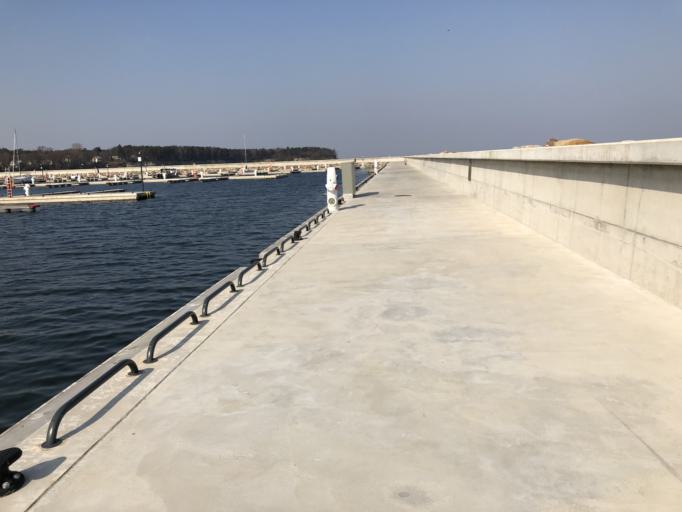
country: EE
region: Harju
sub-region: Harku vald
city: Tabasalu
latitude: 59.4523
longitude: 24.6063
